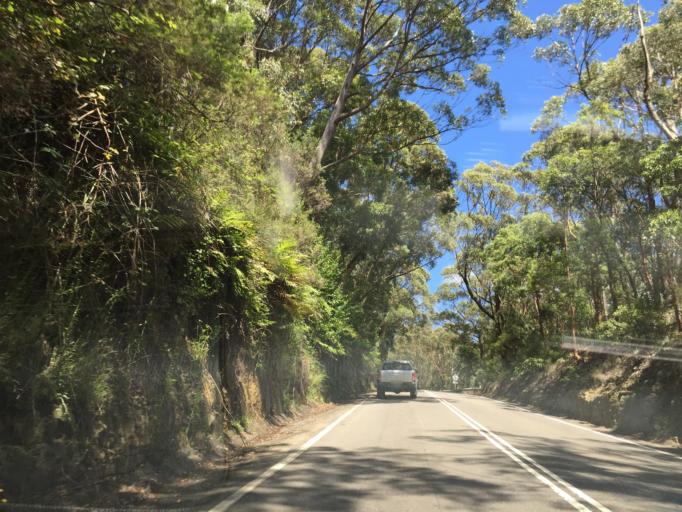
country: AU
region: New South Wales
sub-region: Blue Mountains Municipality
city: Blackheath
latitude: -33.5367
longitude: 150.4212
